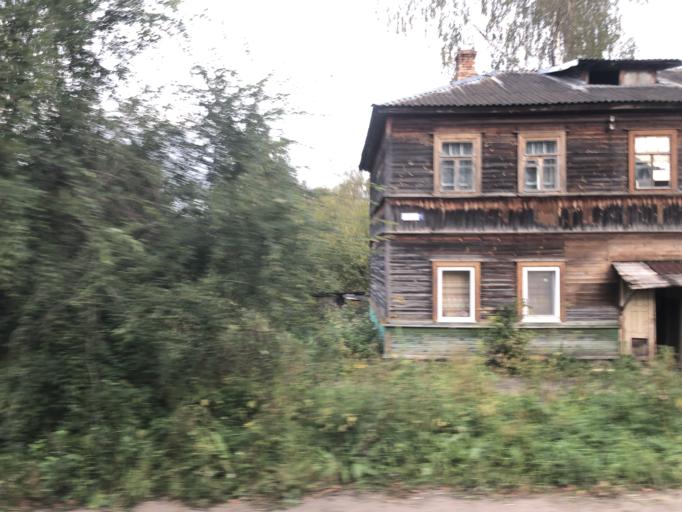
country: RU
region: Tverskaya
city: Rzhev
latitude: 56.2545
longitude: 34.2930
